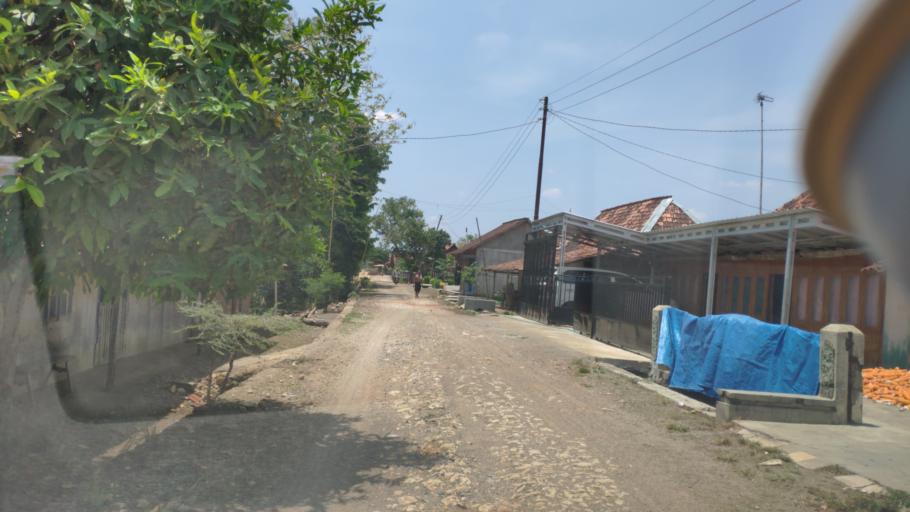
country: ID
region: Central Java
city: Pipes
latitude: -7.0628
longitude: 111.2917
